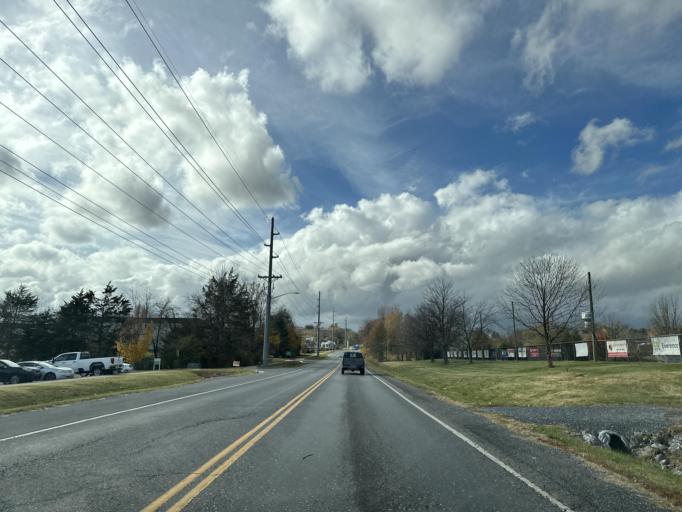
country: US
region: Virginia
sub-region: City of Harrisonburg
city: Harrisonburg
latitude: 38.4684
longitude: -78.8744
